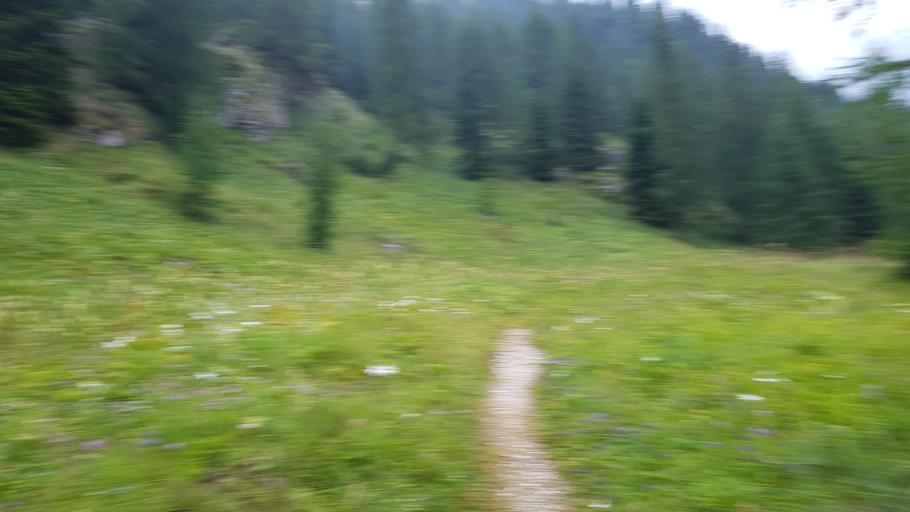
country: SI
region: Kranjska Gora
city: Kranjska Gora
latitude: 46.3564
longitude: 13.7731
